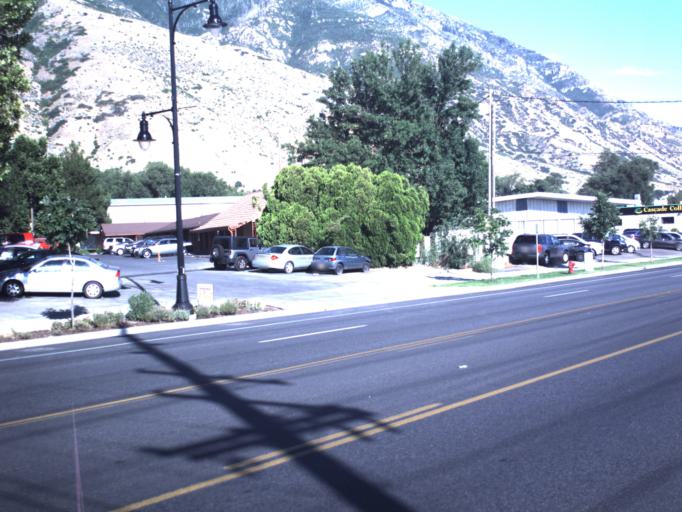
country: US
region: Utah
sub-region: Utah County
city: Provo
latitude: 40.2196
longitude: -111.6390
